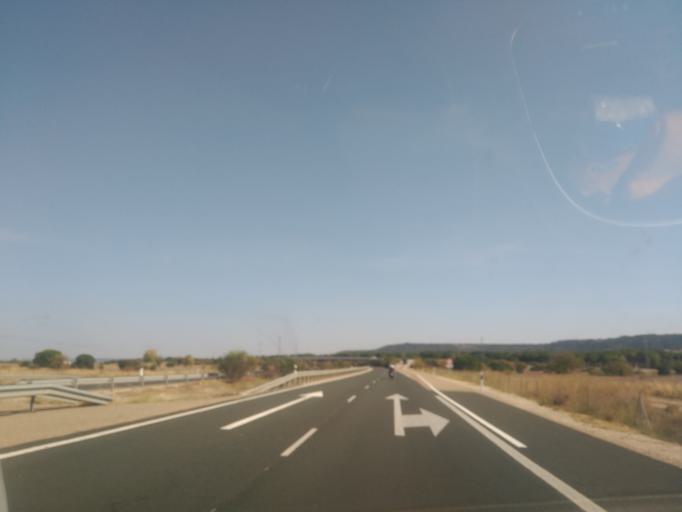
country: ES
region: Castille and Leon
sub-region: Provincia de Valladolid
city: Tudela de Duero
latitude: 41.5883
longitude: -4.5603
